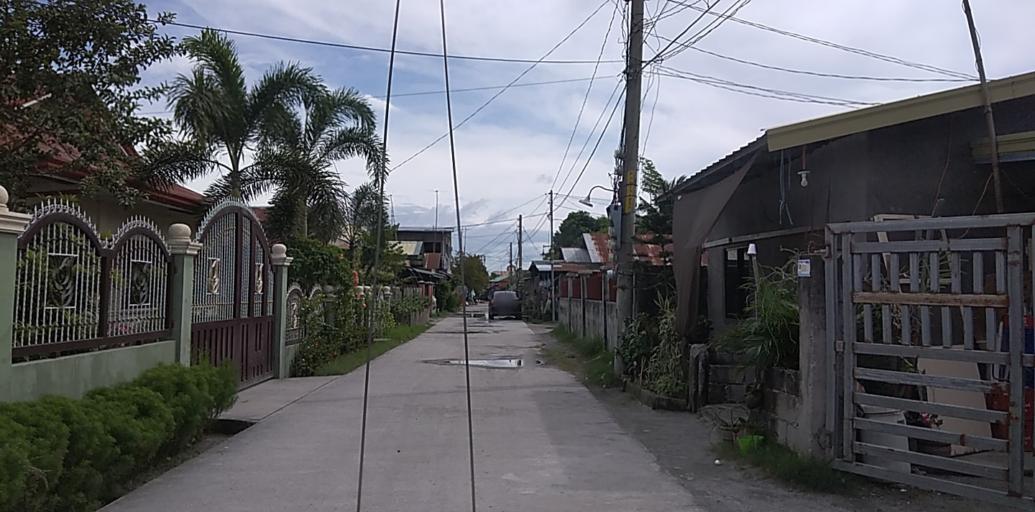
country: PH
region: Central Luzon
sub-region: Province of Pampanga
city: Manibaug Pasig
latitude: 15.1073
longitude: 120.5591
